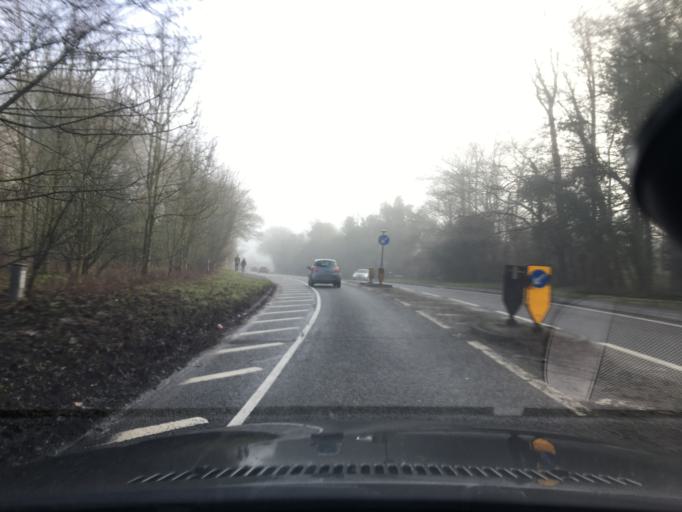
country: GB
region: England
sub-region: Hampshire
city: Old Basing
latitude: 51.2630
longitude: -1.0493
